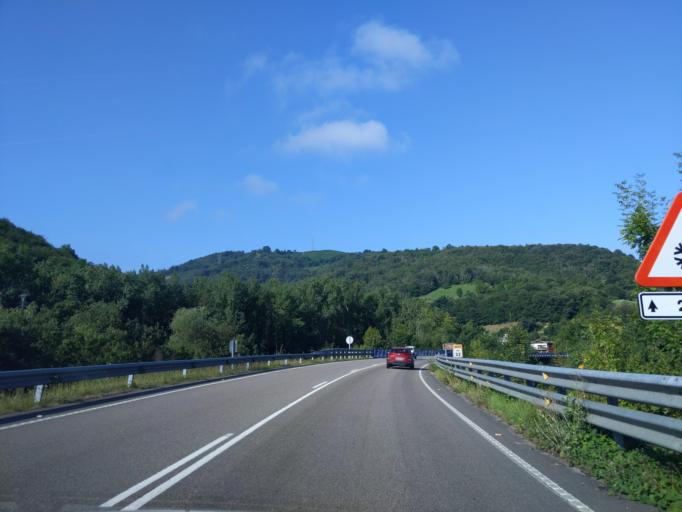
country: ES
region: Asturias
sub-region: Province of Asturias
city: Pola de Laviana
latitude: 43.2331
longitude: -5.5300
